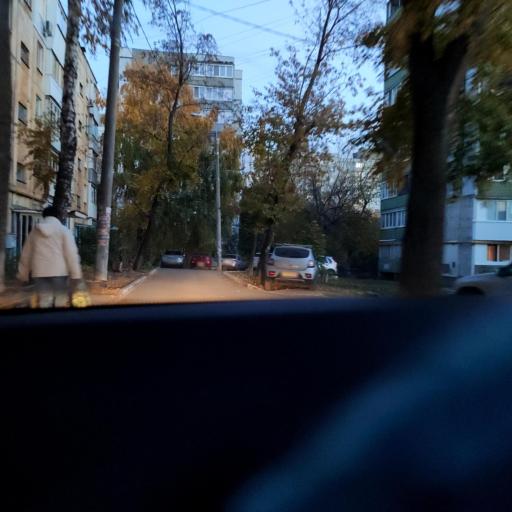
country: RU
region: Samara
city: Samara
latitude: 53.2531
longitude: 50.2440
